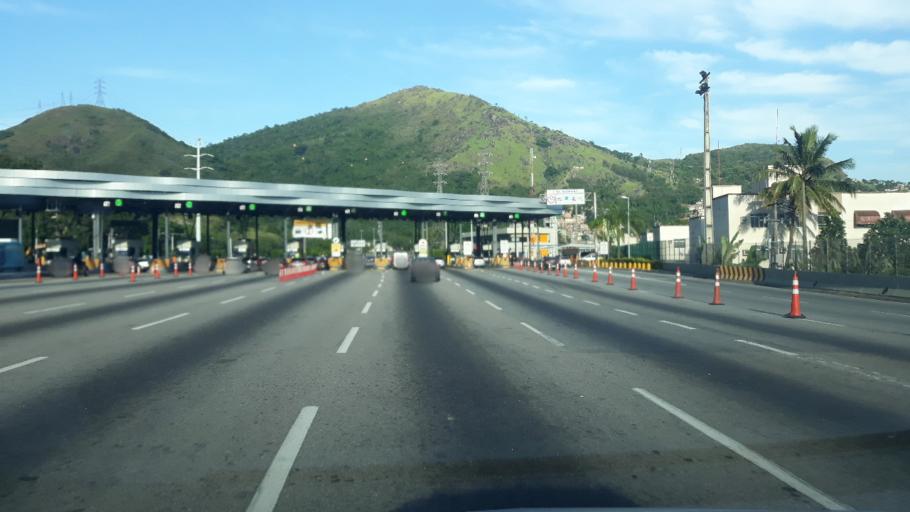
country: BR
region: Rio de Janeiro
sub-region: Rio De Janeiro
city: Rio de Janeiro
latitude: -22.9072
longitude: -43.3081
